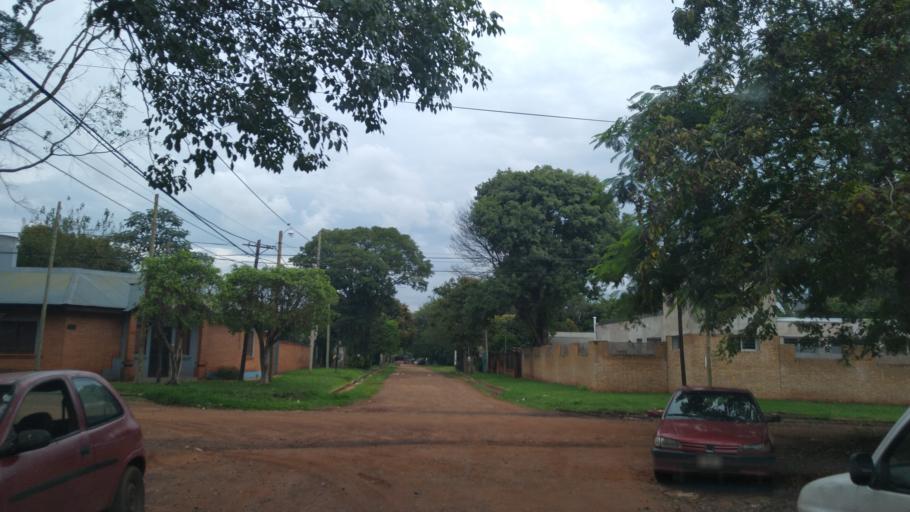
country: AR
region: Misiones
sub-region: Departamento de Capital
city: Posadas
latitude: -27.3719
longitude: -55.9270
